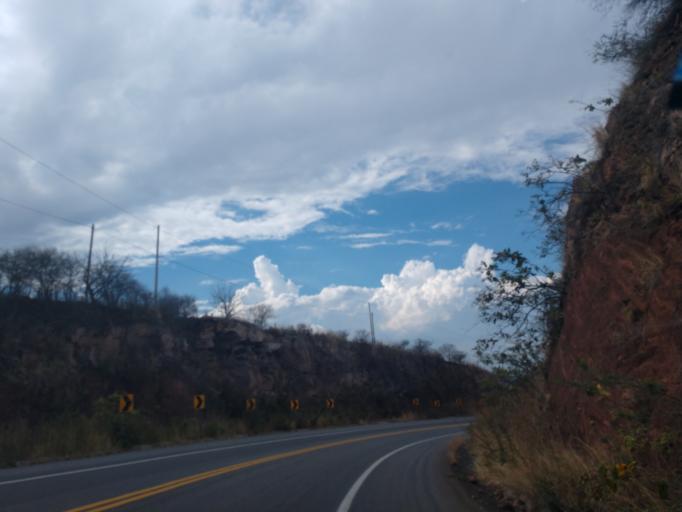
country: MX
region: Jalisco
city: La Manzanilla de la Paz
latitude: 20.1005
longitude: -103.1714
